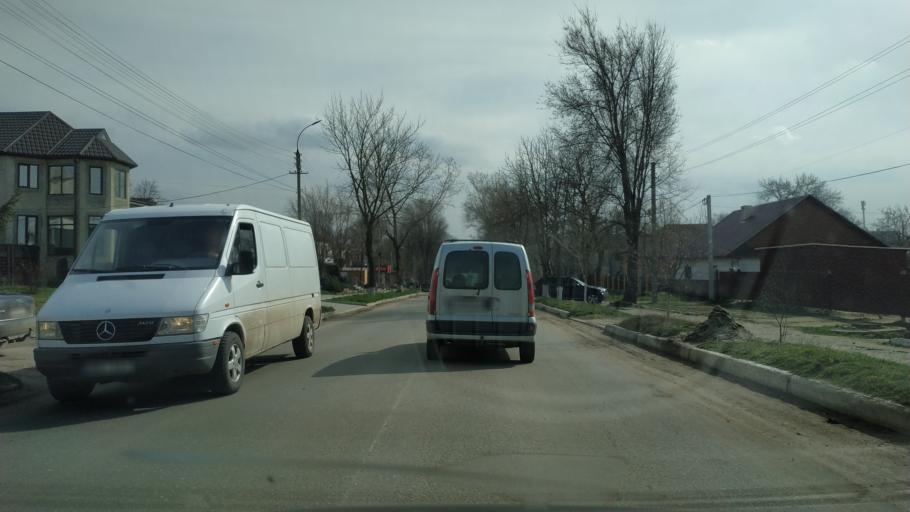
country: MD
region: Gagauzia
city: Vulcanesti
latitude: 45.6868
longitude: 28.4040
